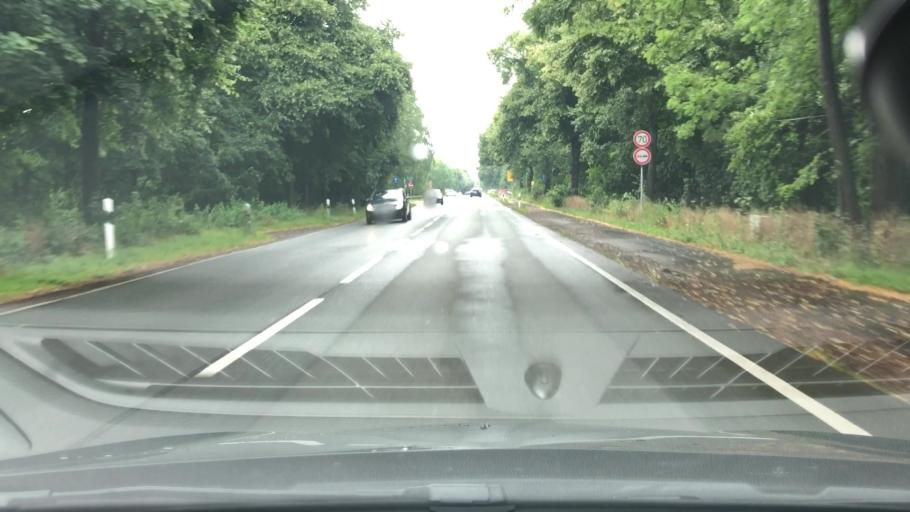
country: DE
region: Lower Saxony
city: Buckeburg
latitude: 52.2610
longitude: 9.0208
